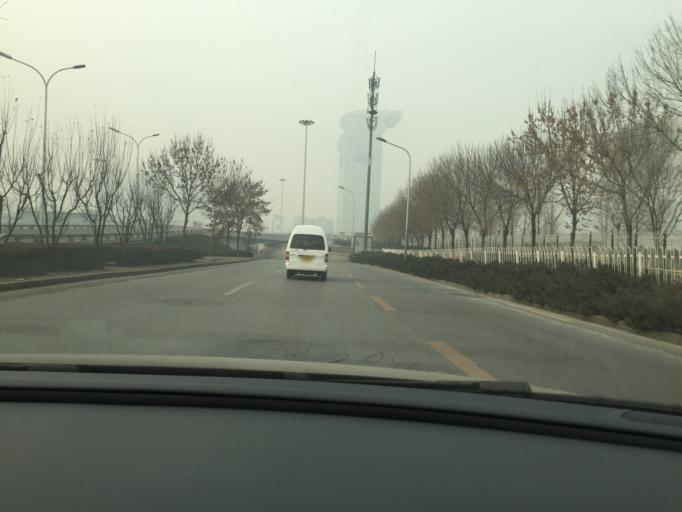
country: CN
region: Beijing
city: Datun
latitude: 39.9871
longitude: 116.3903
